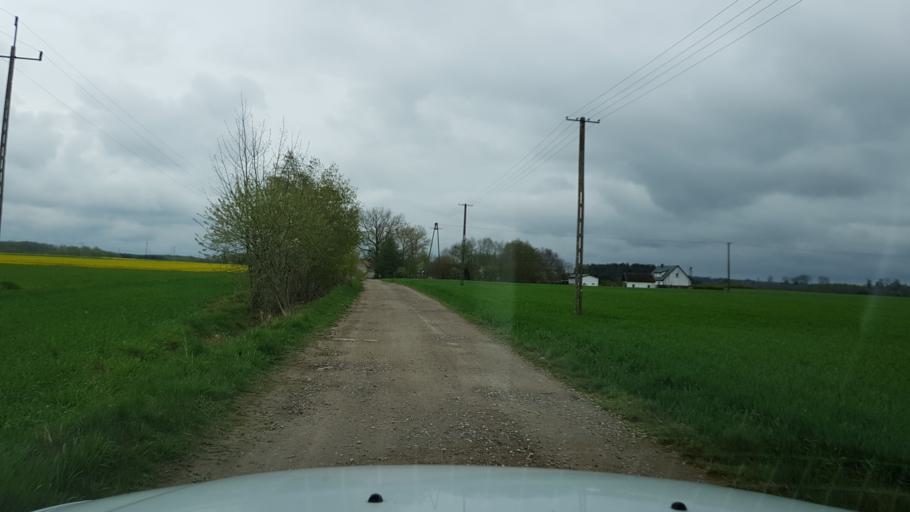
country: PL
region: West Pomeranian Voivodeship
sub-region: Powiat kolobrzeski
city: Ryman
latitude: 54.0344
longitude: 15.4731
